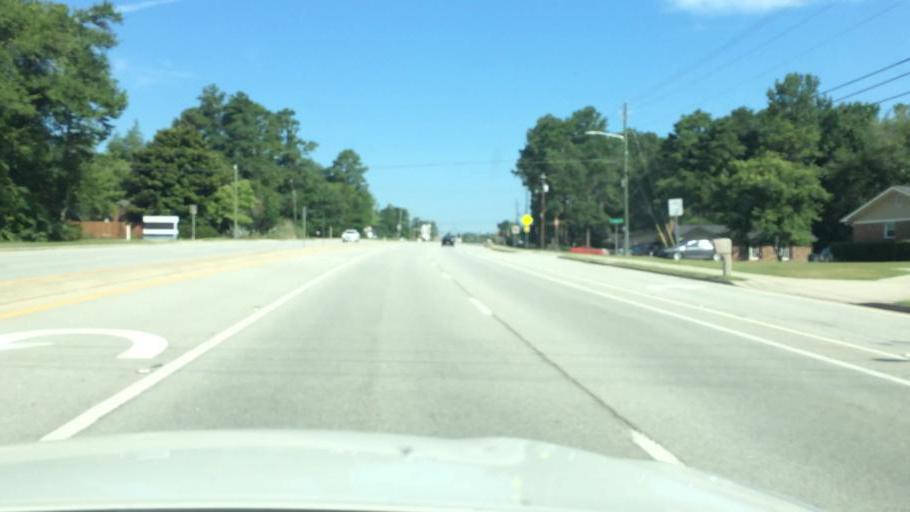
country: US
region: Georgia
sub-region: Columbia County
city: Martinez
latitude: 33.5242
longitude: -82.0683
